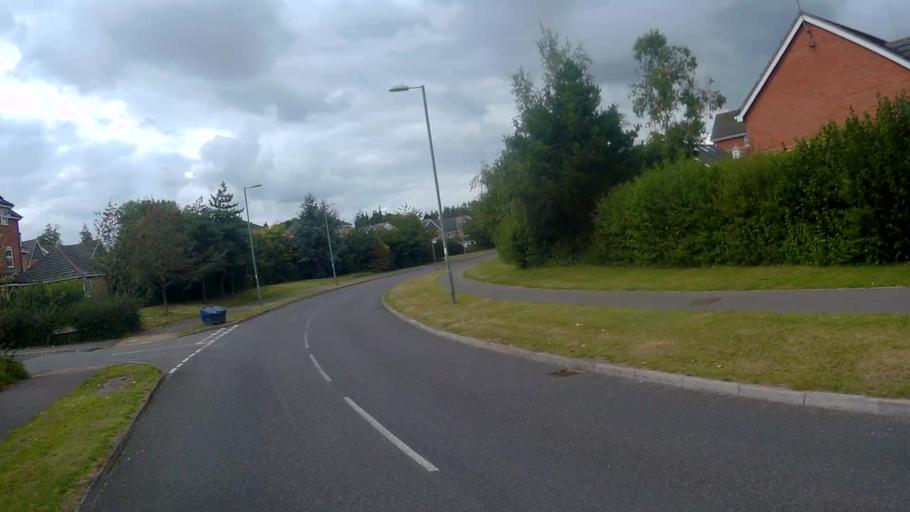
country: GB
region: England
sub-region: Hampshire
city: Basingstoke
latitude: 51.2247
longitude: -1.1411
